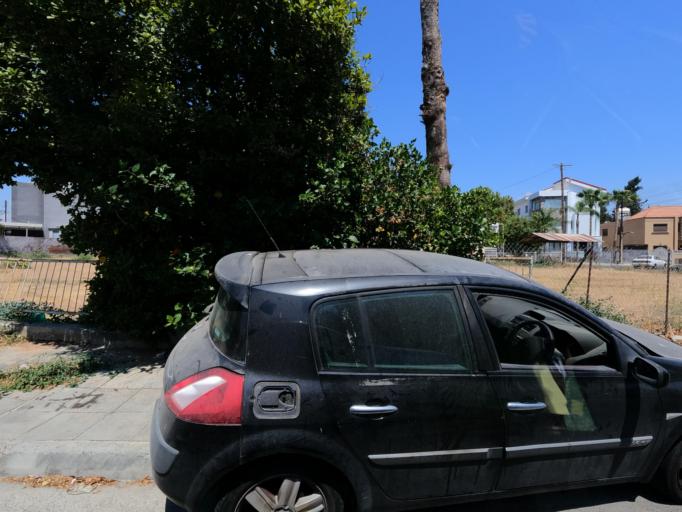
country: CY
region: Limassol
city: Limassol
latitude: 34.6759
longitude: 33.0180
